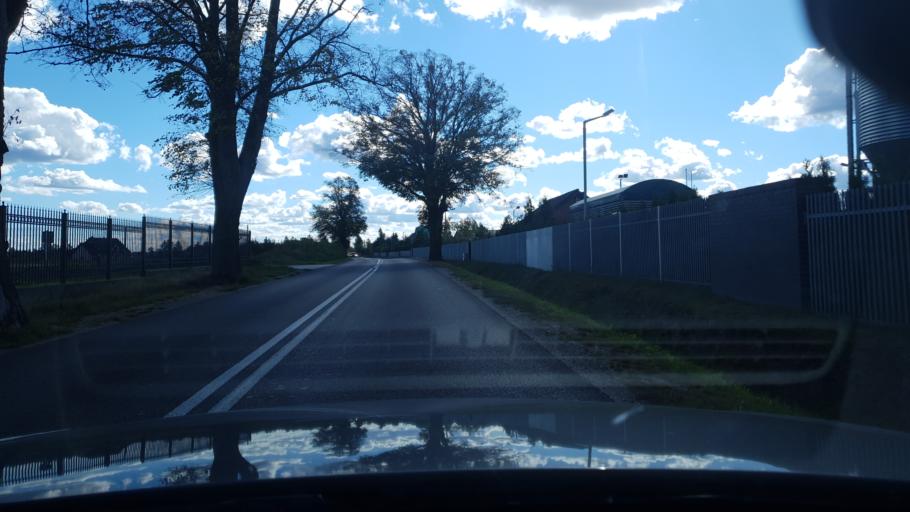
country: PL
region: Pomeranian Voivodeship
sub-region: Powiat pucki
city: Zelistrzewo
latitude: 54.6971
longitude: 18.4116
